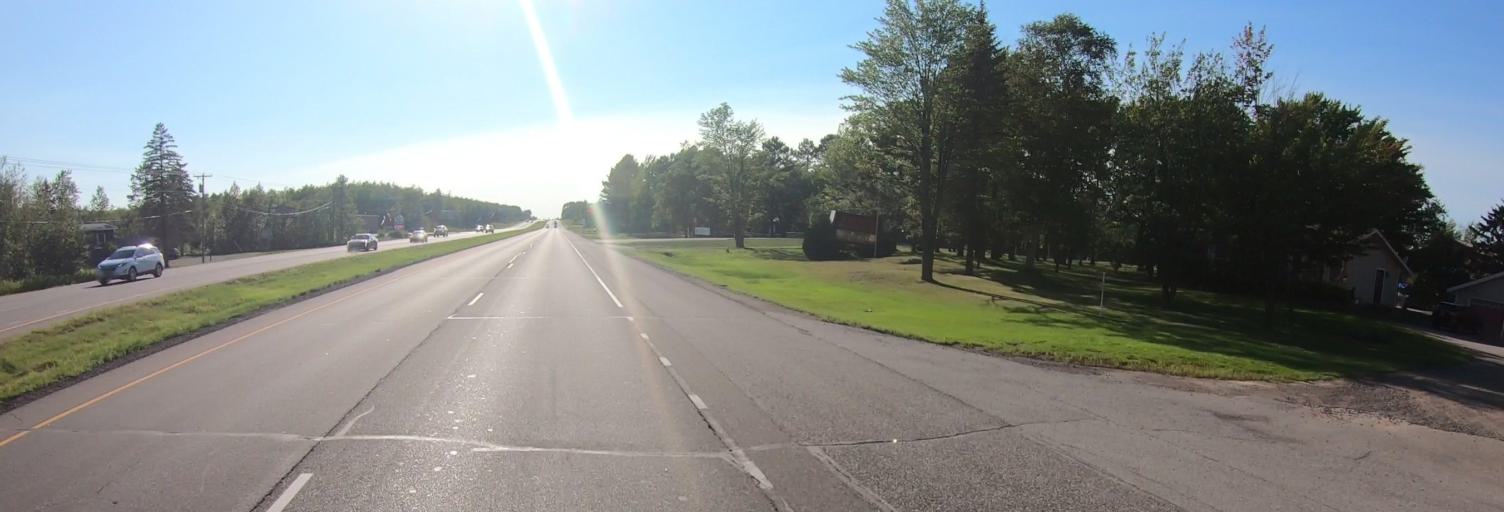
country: US
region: Minnesota
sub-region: Saint Louis County
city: Hermantown
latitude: 46.8367
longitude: -92.2191
